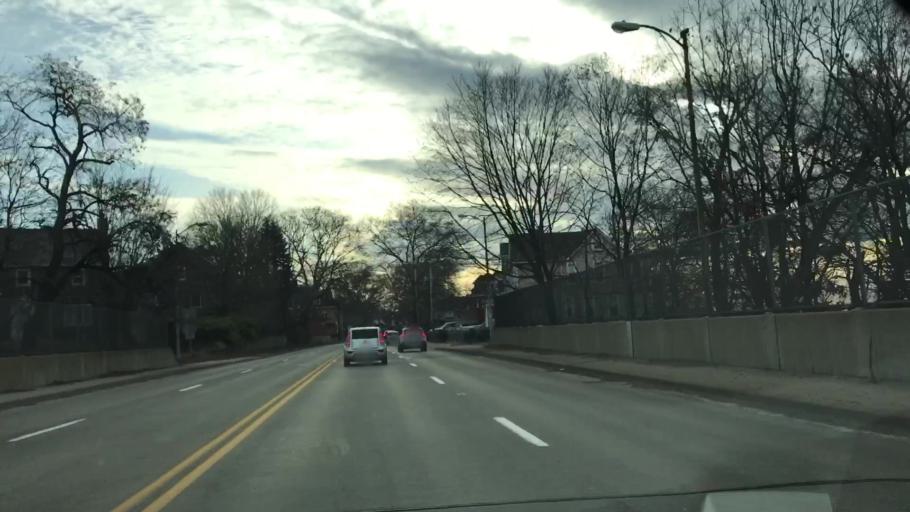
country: US
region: Pennsylvania
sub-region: Allegheny County
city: Ben Avon
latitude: 40.5027
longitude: -80.0784
